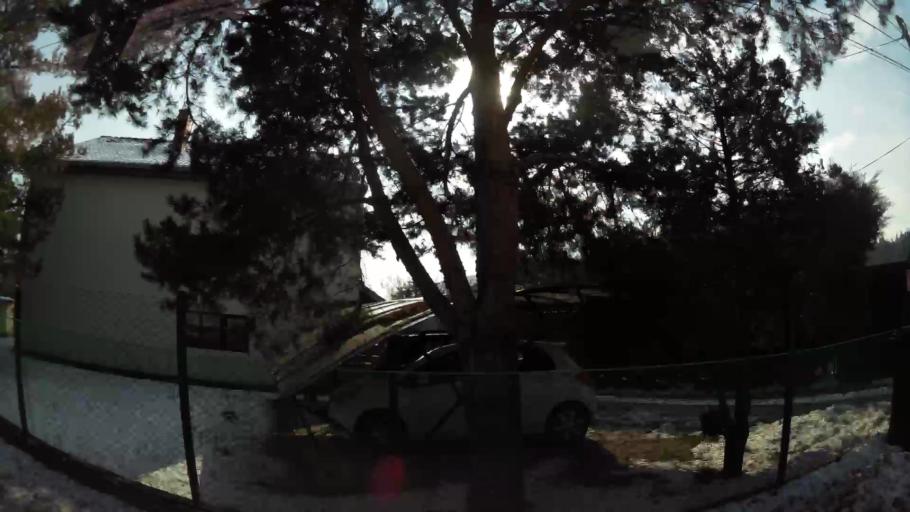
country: MK
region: Suto Orizari
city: Suto Orizare
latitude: 42.0296
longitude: 21.3796
